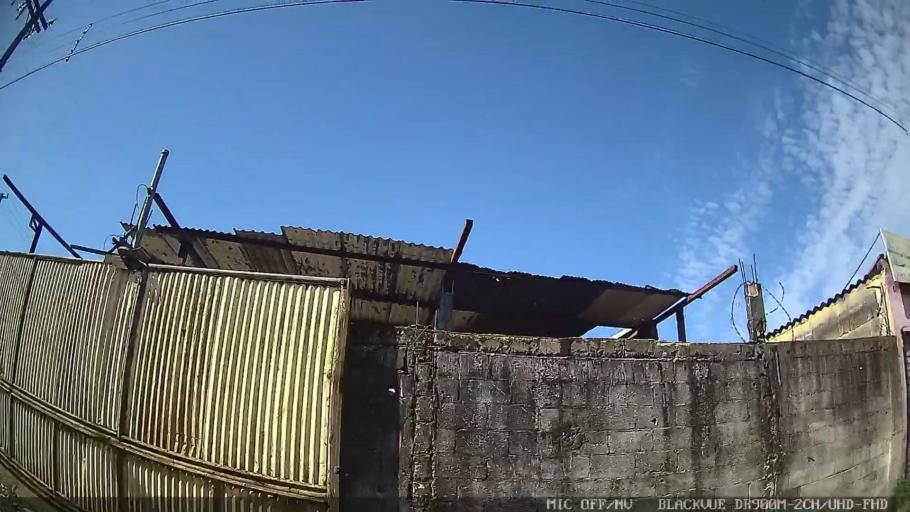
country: BR
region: Sao Paulo
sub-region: Guaruja
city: Guaruja
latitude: -23.9618
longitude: -46.2747
